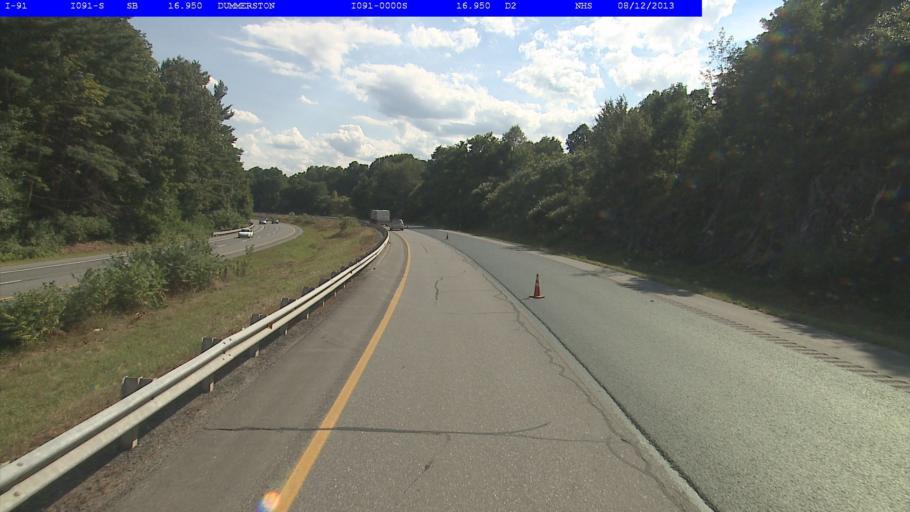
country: US
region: New Hampshire
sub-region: Cheshire County
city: Chesterfield
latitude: 42.9523
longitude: -72.5358
